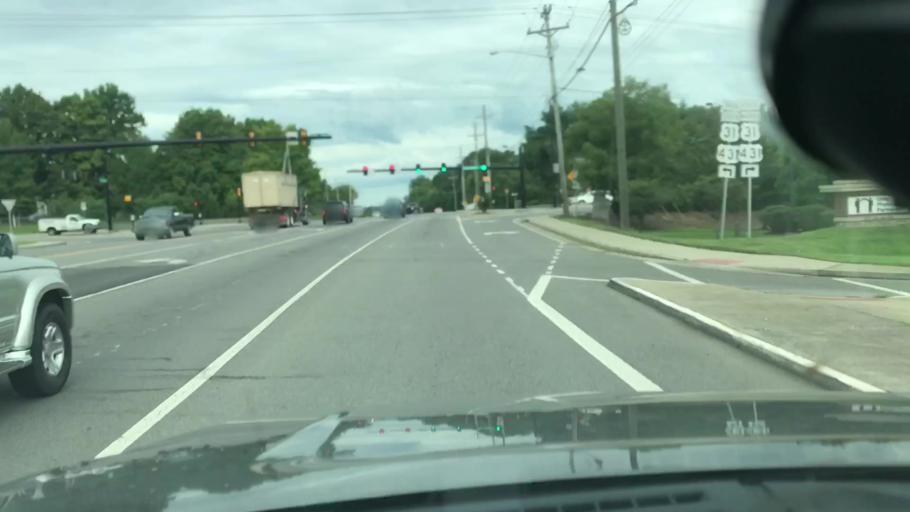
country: US
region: Tennessee
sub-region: Williamson County
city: Franklin
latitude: 35.9171
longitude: -86.8435
